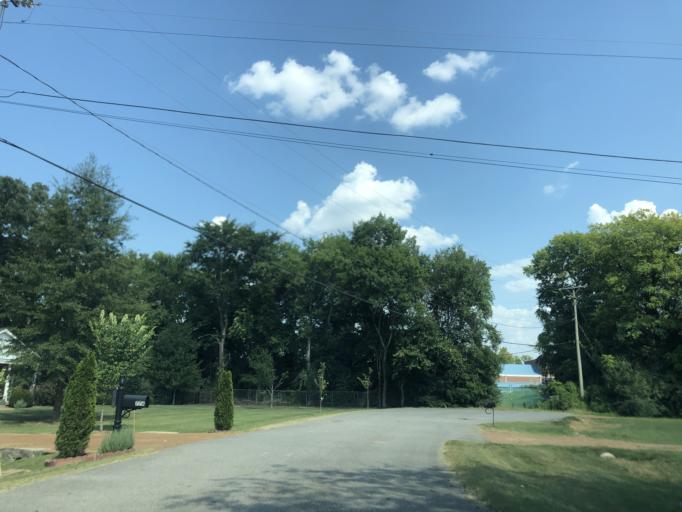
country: US
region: Tennessee
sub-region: Davidson County
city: Oak Hill
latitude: 36.0972
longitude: -86.7689
